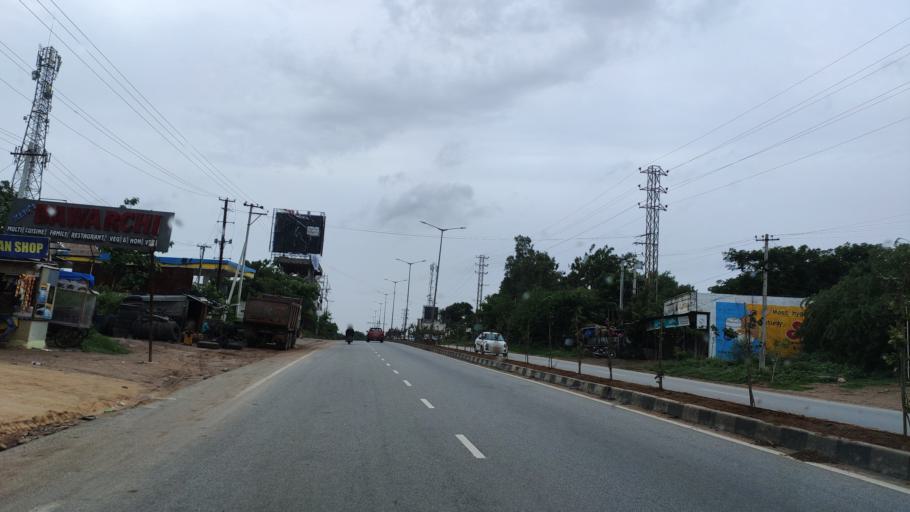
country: IN
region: Telangana
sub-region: Rangareddi
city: Secunderabad
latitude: 17.5925
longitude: 78.5702
